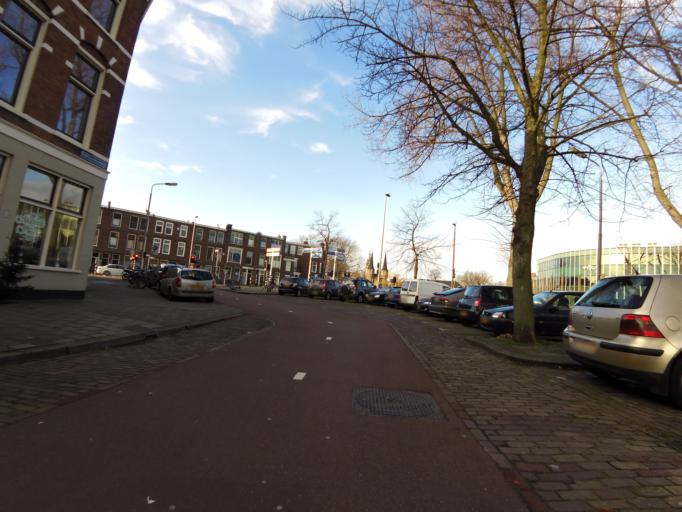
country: NL
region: South Holland
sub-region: Gemeente Delft
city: Delft
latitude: 52.0104
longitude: 4.3712
